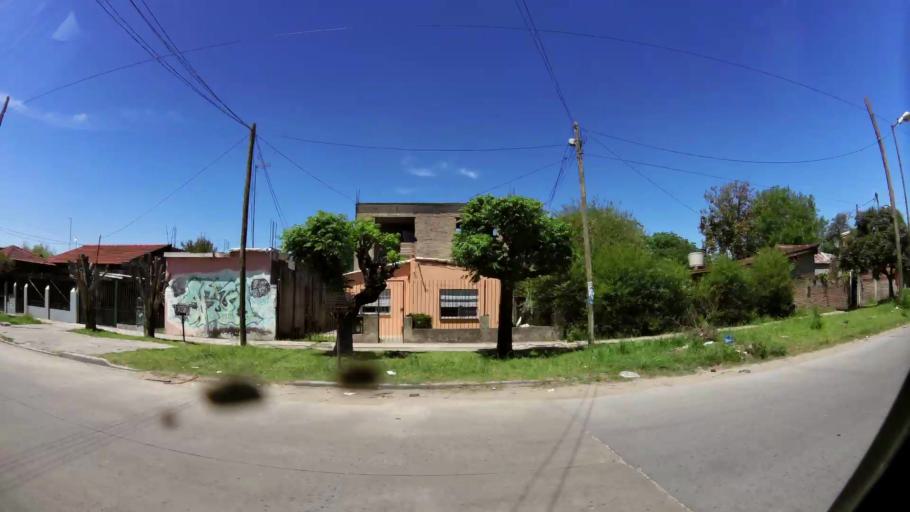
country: AR
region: Buenos Aires
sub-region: Partido de Quilmes
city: Quilmes
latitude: -34.7178
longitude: -58.3236
